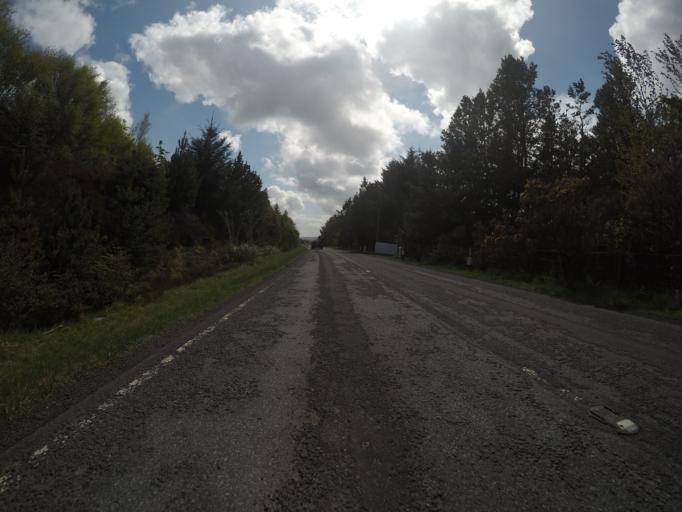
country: GB
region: Scotland
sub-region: Highland
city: Portree
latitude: 57.5700
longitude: -6.3645
